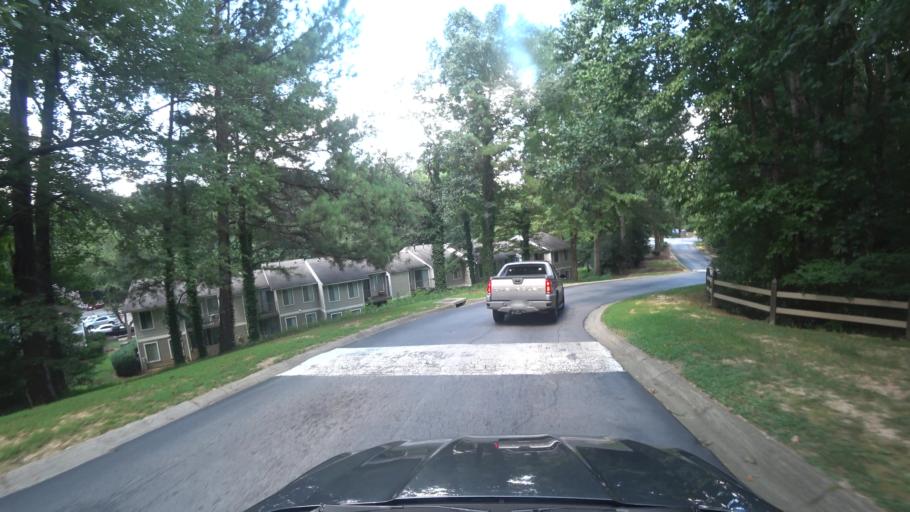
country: US
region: Georgia
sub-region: Gwinnett County
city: Norcross
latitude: 33.9541
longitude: -84.2532
